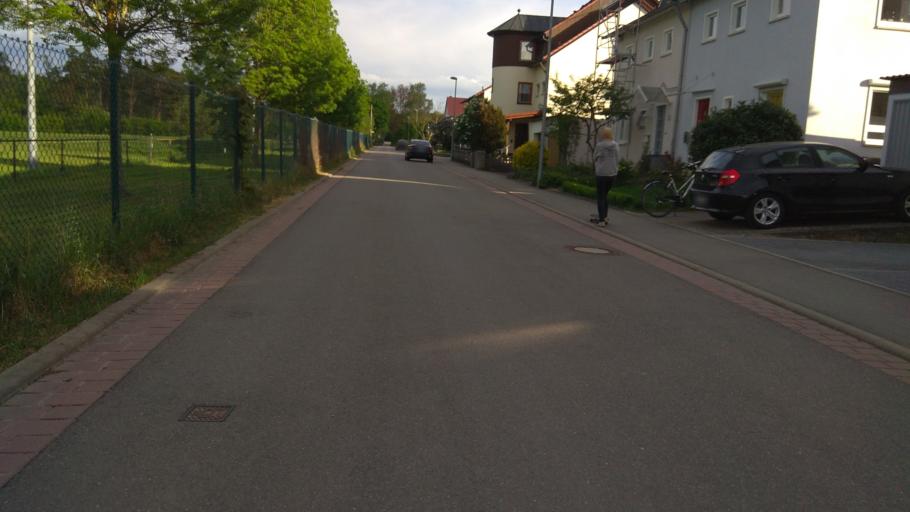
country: DE
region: Baden-Wuerttemberg
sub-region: Tuebingen Region
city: Wannweil
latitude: 48.5106
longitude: 9.1563
